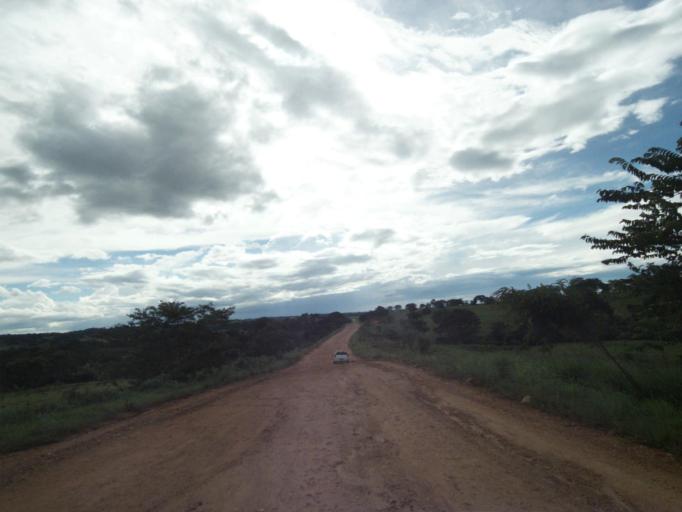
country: BR
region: Goias
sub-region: Jaragua
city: Jaragua
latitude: -15.8430
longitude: -49.3338
